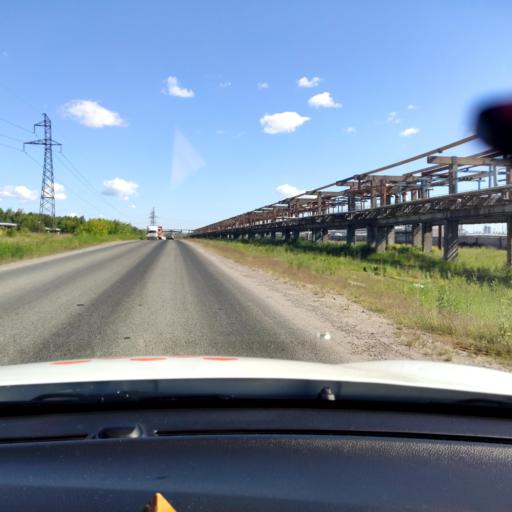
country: RU
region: Tatarstan
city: Staroye Arakchino
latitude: 55.8729
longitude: 48.9745
